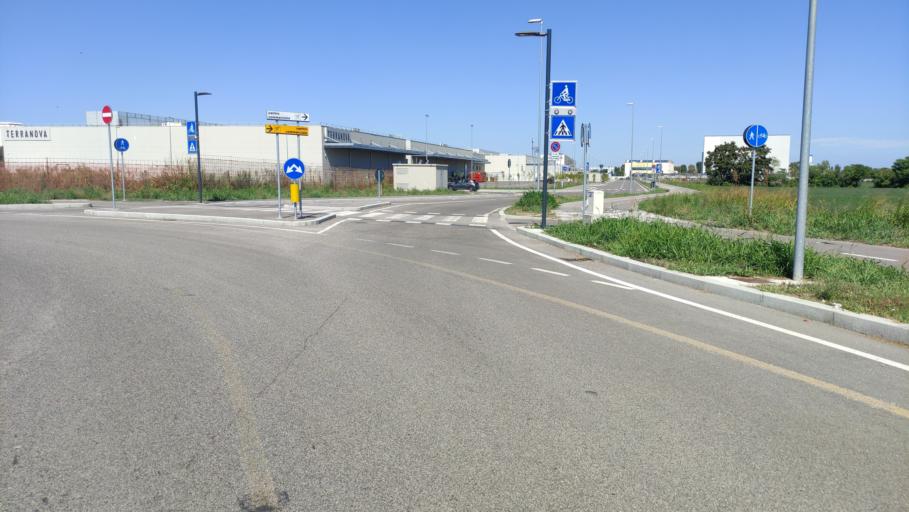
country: IT
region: Emilia-Romagna
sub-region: Provincia di Ravenna
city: Porto Fuori
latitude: 44.4204
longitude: 12.2349
